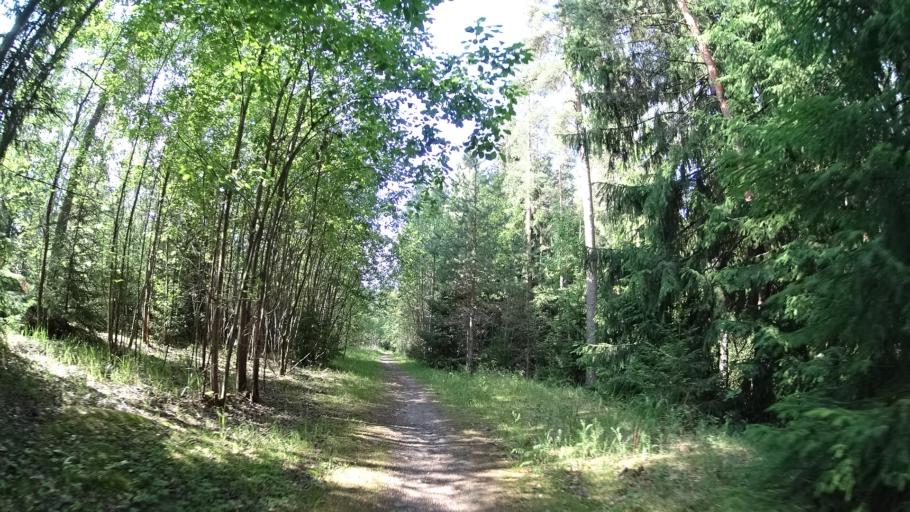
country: FI
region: Uusimaa
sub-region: Helsinki
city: Teekkarikylae
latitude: 60.2908
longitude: 24.9033
